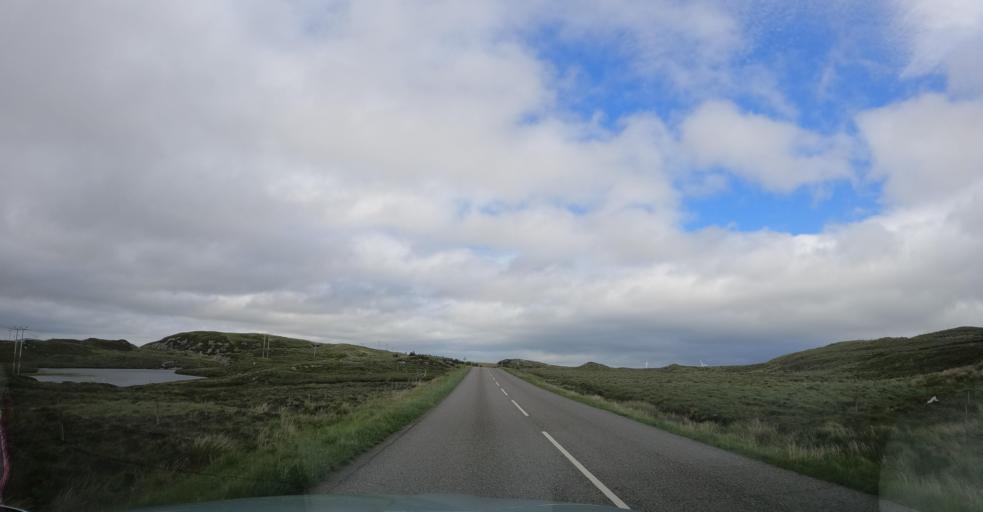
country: GB
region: Scotland
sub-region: Eilean Siar
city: Stornoway
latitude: 58.1723
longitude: -6.4742
